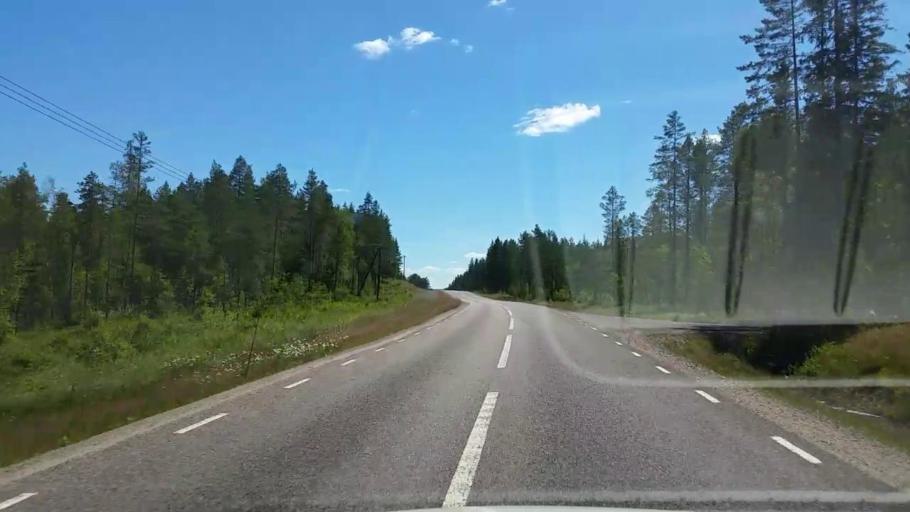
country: SE
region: Gaevleborg
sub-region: Ovanakers Kommun
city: Edsbyn
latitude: 61.5070
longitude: 15.6831
